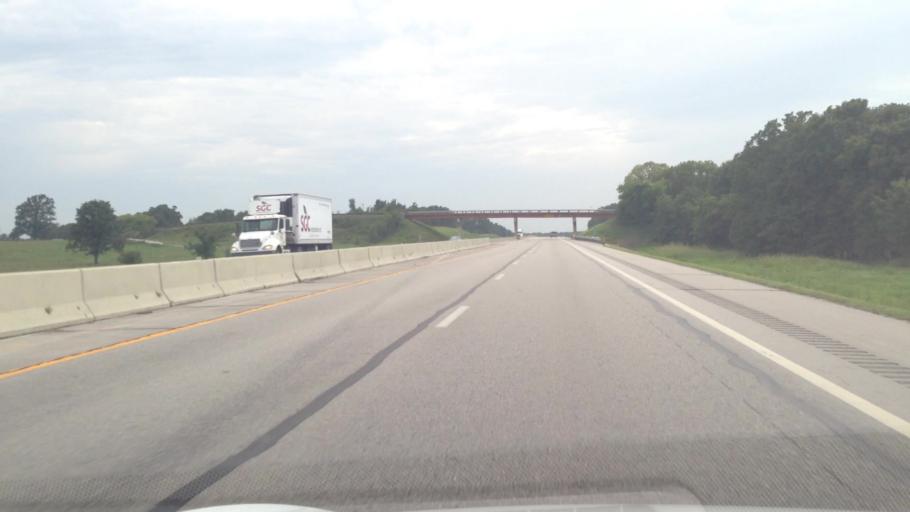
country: US
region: Kansas
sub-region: Cherokee County
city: Baxter Springs
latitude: 36.9505
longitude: -94.6758
